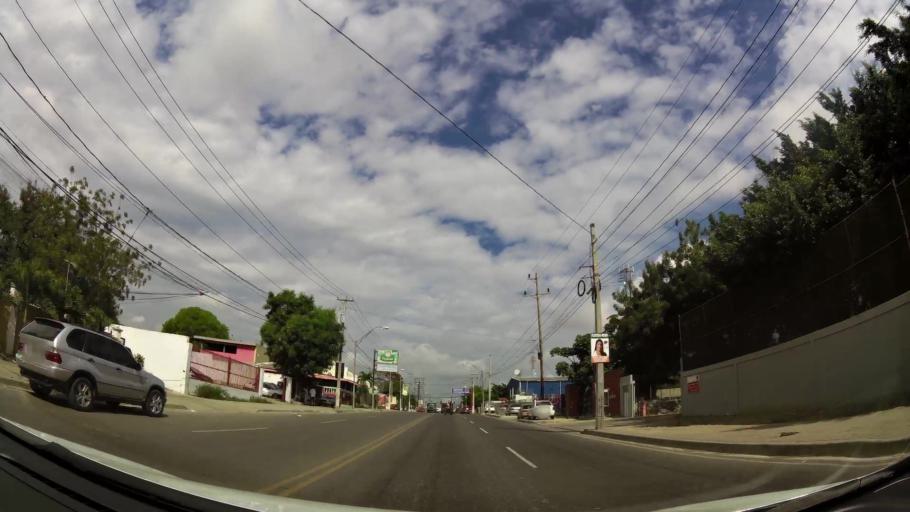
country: DO
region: Santiago
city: Santiago de los Caballeros
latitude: 19.4812
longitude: -70.7276
